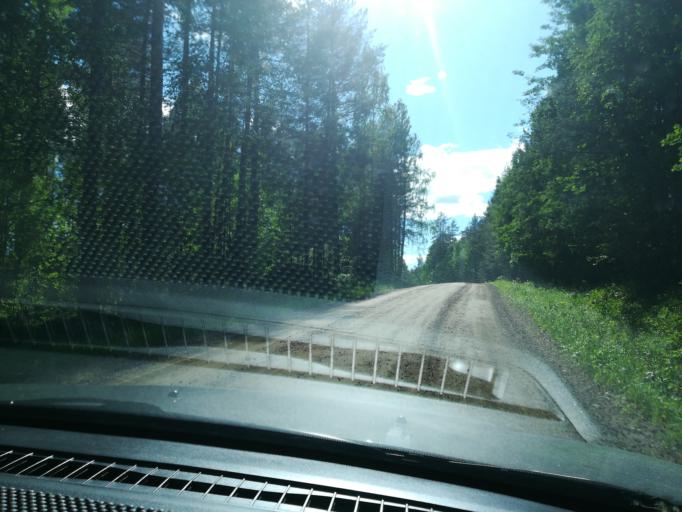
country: FI
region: Southern Savonia
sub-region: Mikkeli
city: Puumala
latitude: 61.6623
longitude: 28.1411
